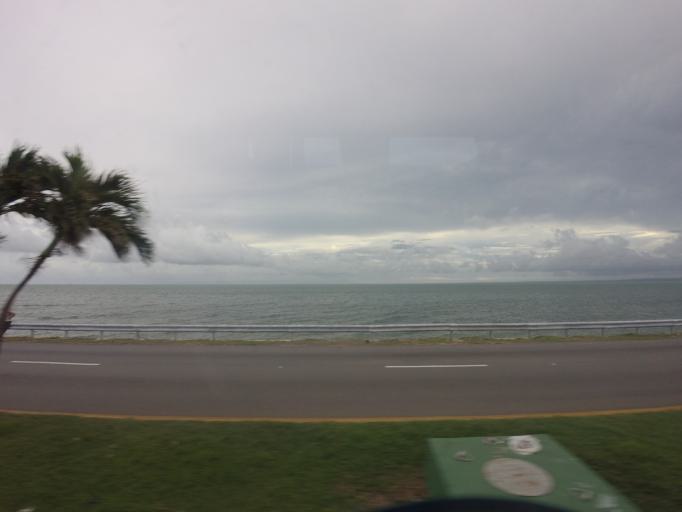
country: CU
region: Matanzas
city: Varadero
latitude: 23.1700
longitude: -81.2127
